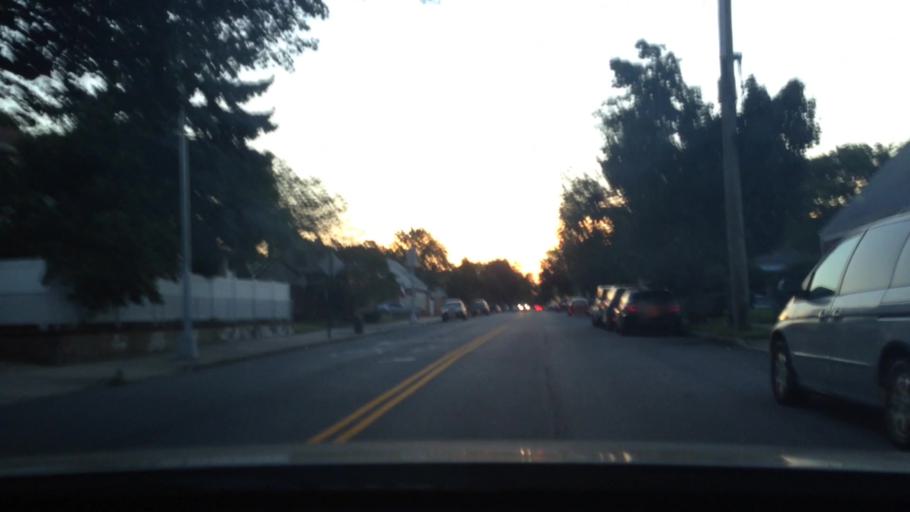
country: US
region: New York
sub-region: Nassau County
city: Bellerose
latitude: 40.7424
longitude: -73.7129
